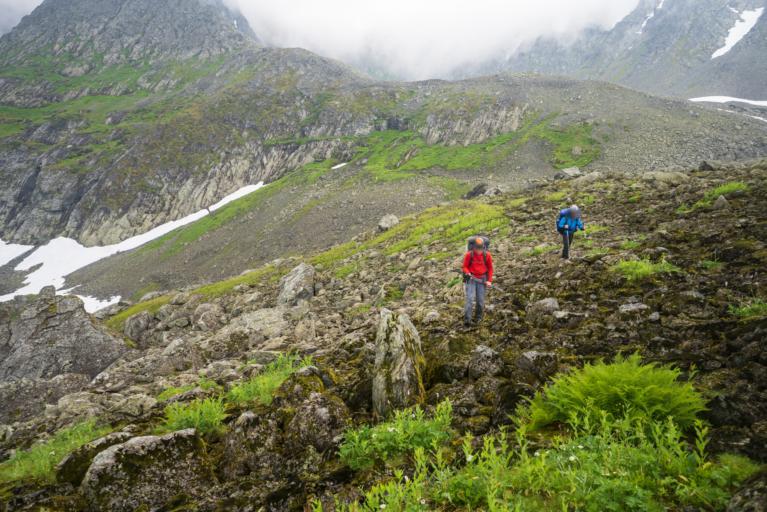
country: RU
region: Komi Republic
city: Synya
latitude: 64.7869
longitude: 58.9132
